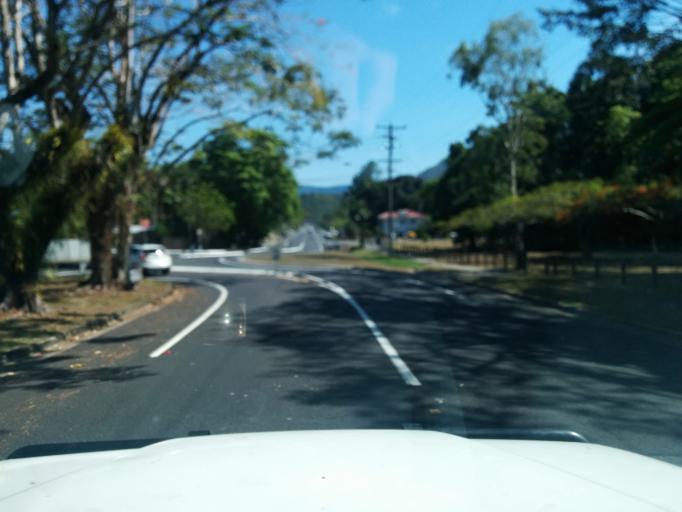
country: AU
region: Queensland
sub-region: Cairns
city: Redlynch
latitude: -16.9020
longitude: 145.7289
